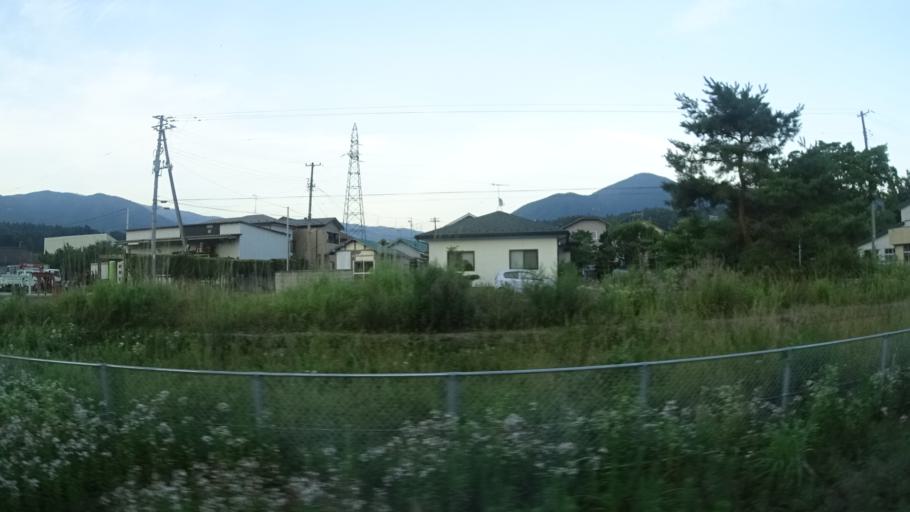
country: JP
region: Fukushima
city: Funehikimachi-funehiki
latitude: 37.3253
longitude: 140.6597
